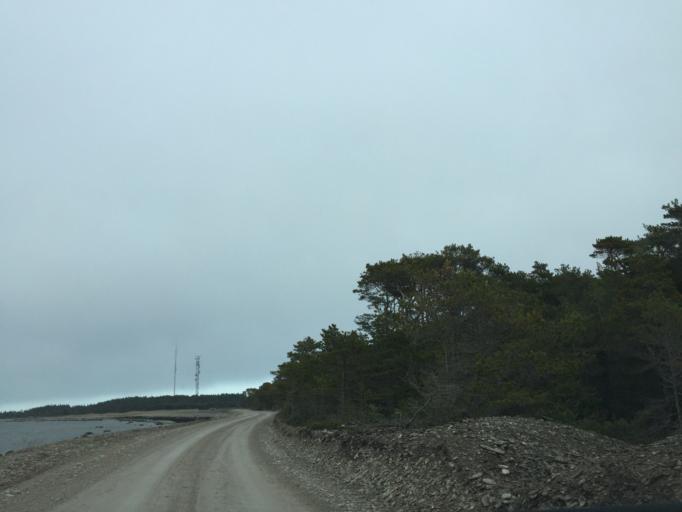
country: EE
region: Saare
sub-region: Kuressaare linn
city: Kuressaare
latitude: 58.5089
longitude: 21.9133
